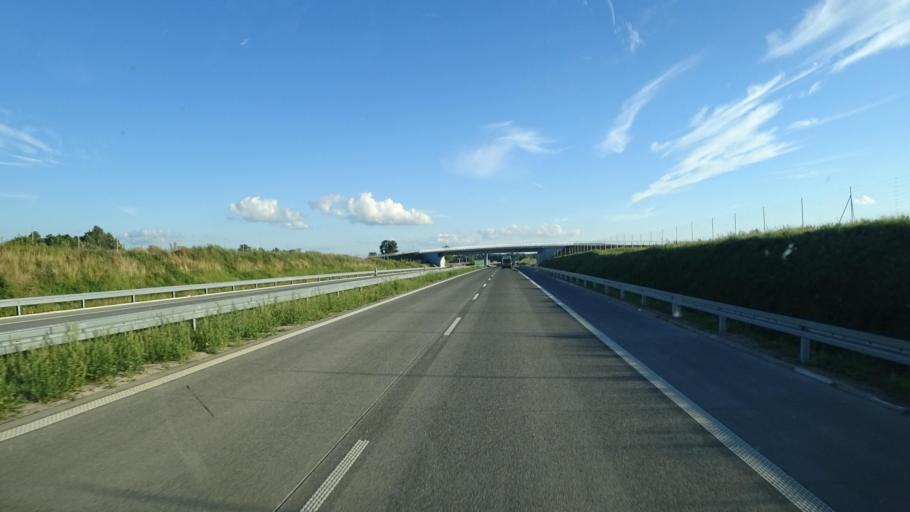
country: PL
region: Podlasie
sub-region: Powiat suwalski
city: Raczki
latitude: 53.9447
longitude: 22.7647
